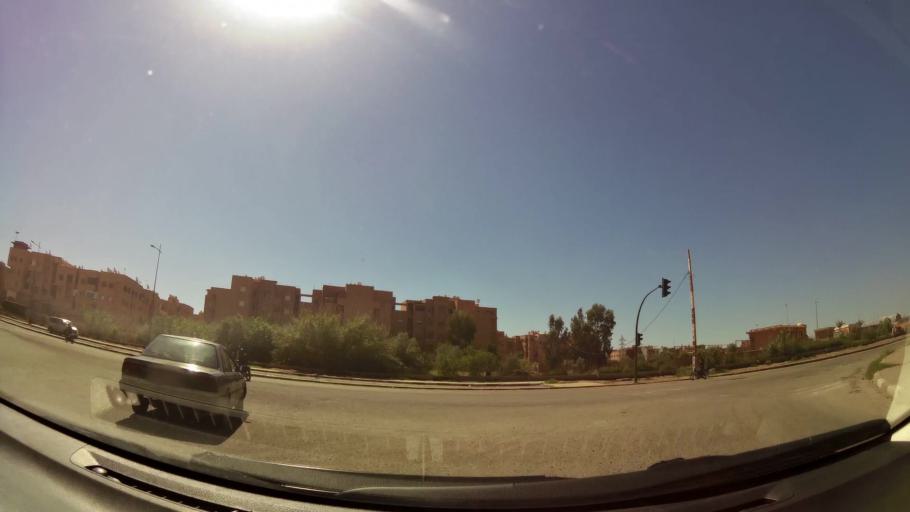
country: MA
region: Marrakech-Tensift-Al Haouz
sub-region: Marrakech
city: Marrakesh
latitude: 31.5774
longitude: -8.0626
